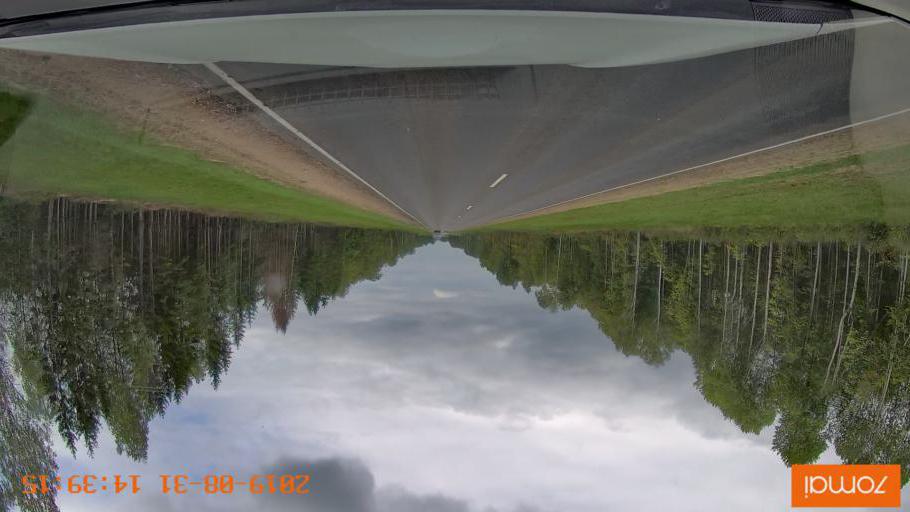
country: RU
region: Smolensk
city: Yekimovichi
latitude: 54.1903
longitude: 33.5482
